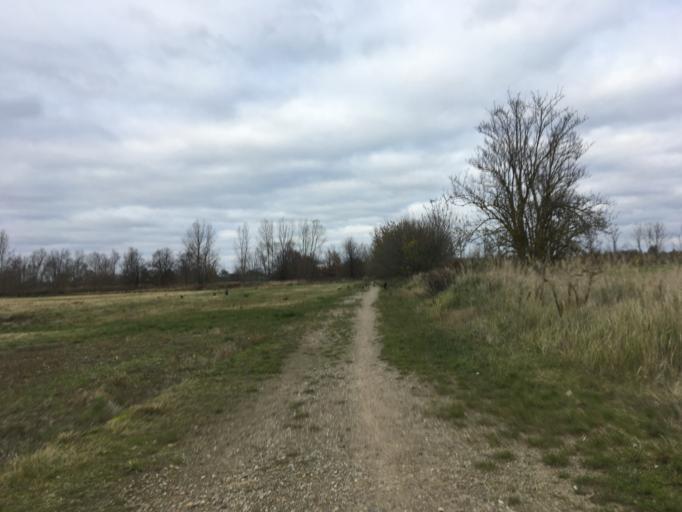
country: DE
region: Berlin
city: Bohnsdorf
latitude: 52.3935
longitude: 13.5527
